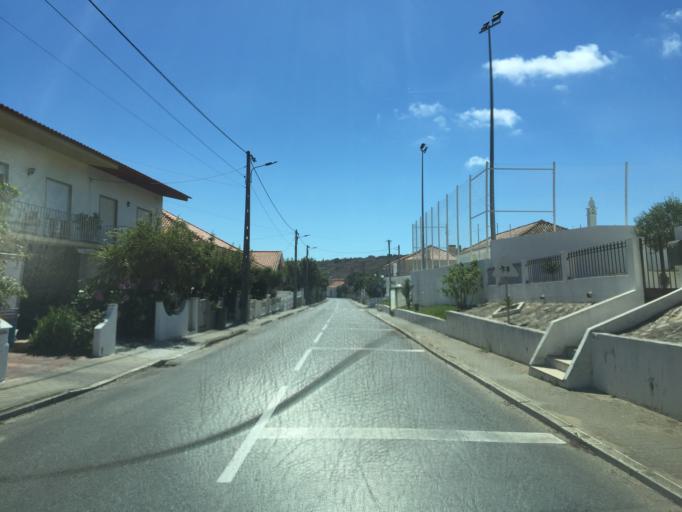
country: PT
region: Lisbon
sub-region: Torres Vedras
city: A dos Cunhados
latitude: 39.1822
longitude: -9.3134
